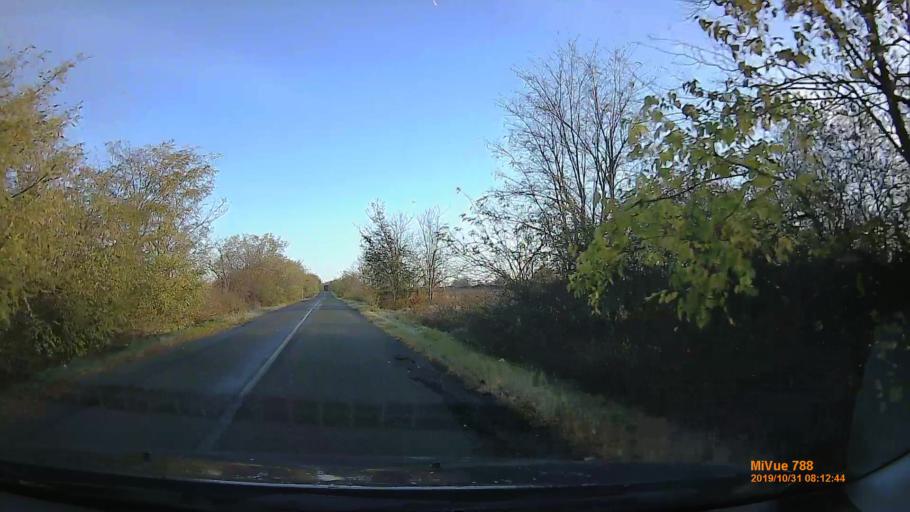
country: HU
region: Pest
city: Pilis
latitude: 47.3282
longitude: 19.5672
